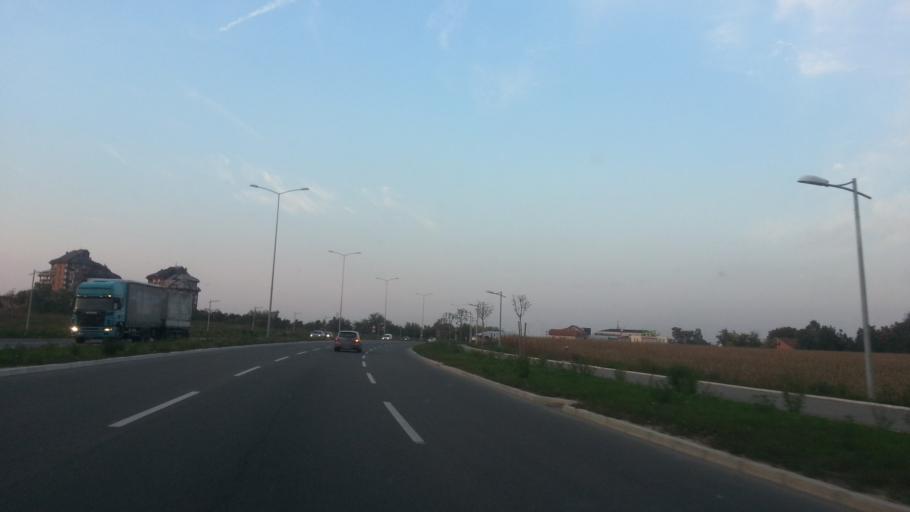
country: RS
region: Central Serbia
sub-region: Belgrade
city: Zemun
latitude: 44.8552
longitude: 20.3739
